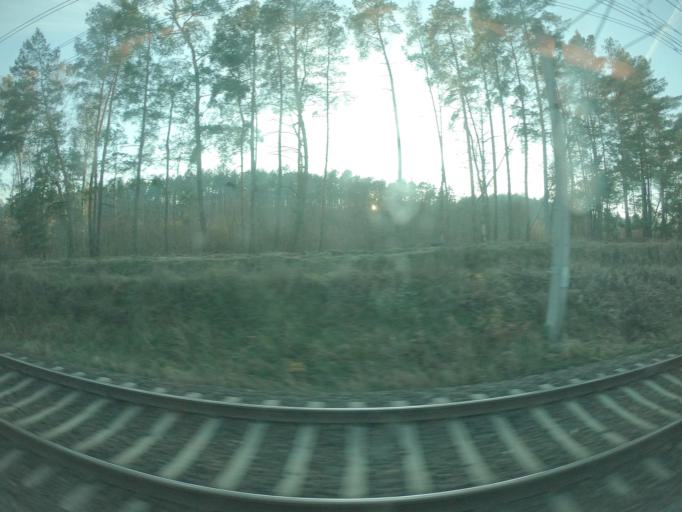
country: PL
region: Lubusz
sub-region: Powiat slubicki
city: Rzepin
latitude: 52.2677
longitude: 14.9315
